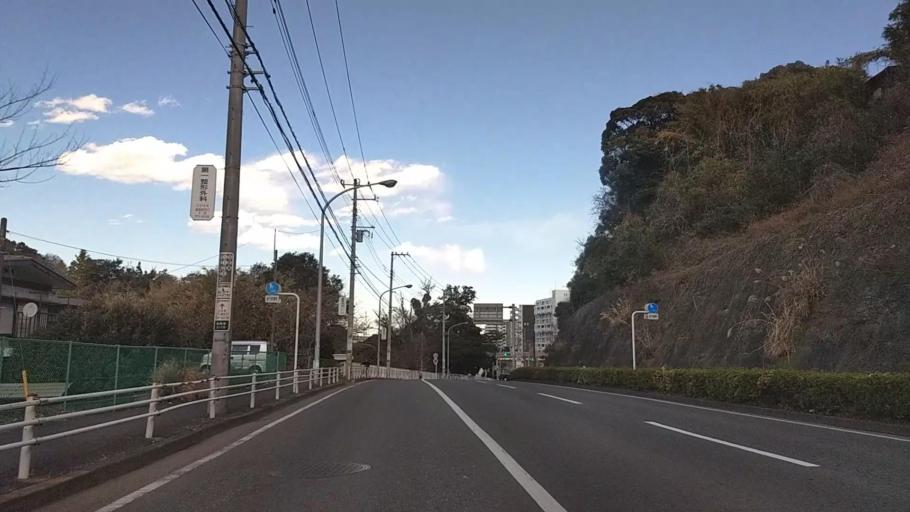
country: JP
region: Kanagawa
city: Yokohama
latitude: 35.3725
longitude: 139.6339
